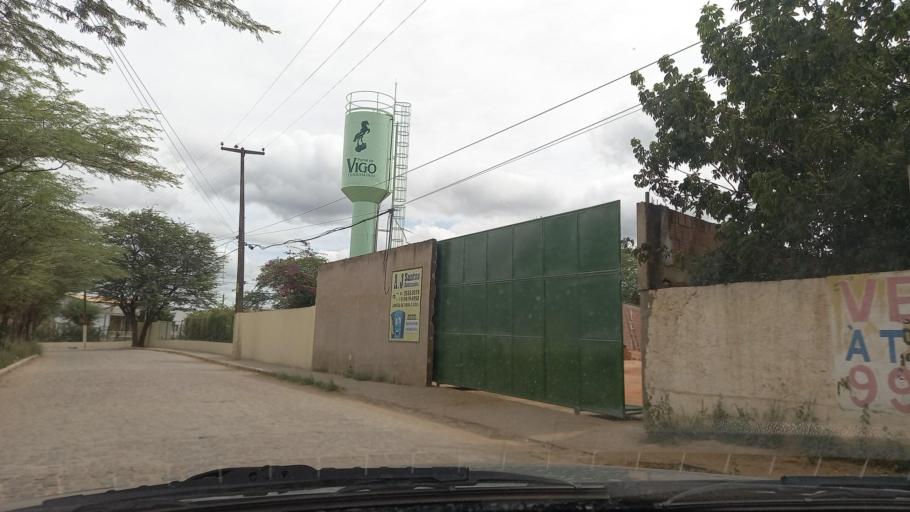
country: ET
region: Oromiya
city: Gore
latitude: 8.1944
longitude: 35.5744
